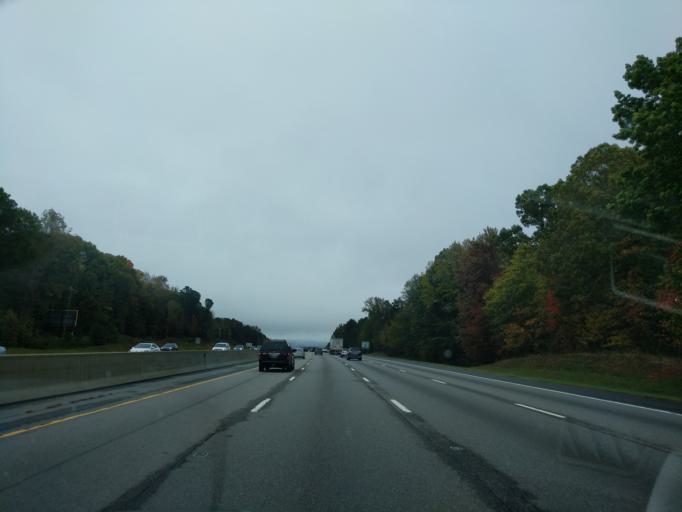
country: US
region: North Carolina
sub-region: Orange County
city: Hillsborough
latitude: 36.0741
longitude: -79.1830
